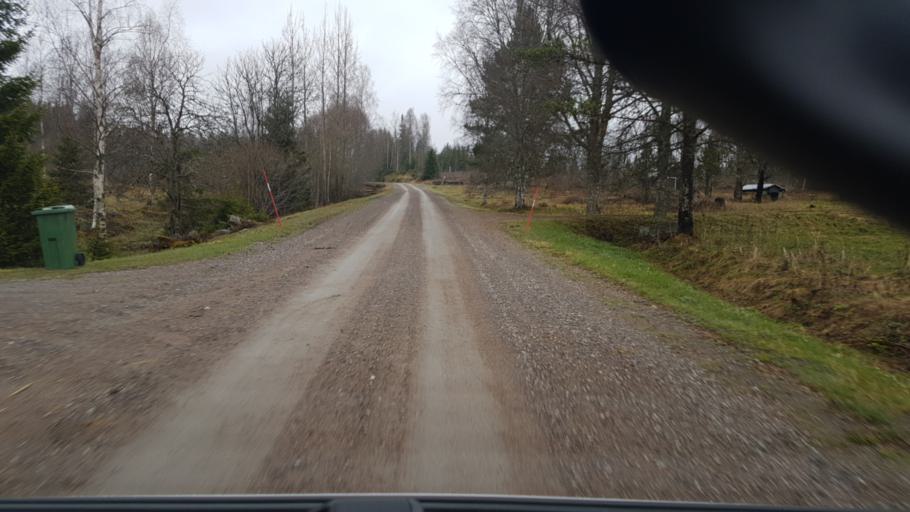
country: SE
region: Vaermland
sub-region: Eda Kommun
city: Charlottenberg
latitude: 59.9951
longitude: 12.5081
